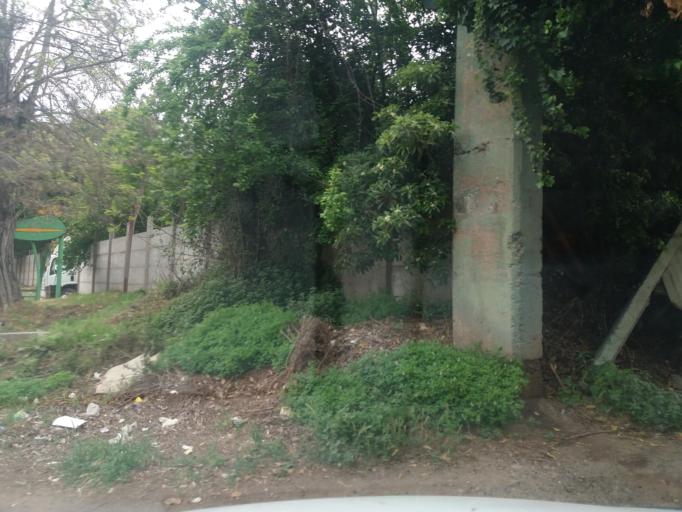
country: CL
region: Valparaiso
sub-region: Provincia de Quillota
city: Hacienda La Calera
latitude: -32.8281
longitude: -71.1244
